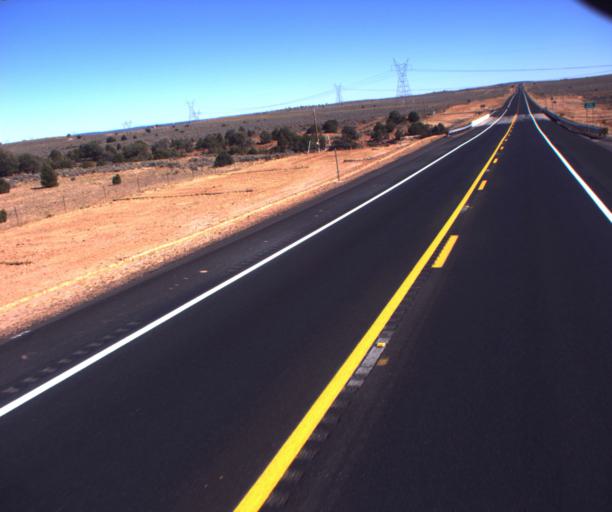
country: US
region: Arizona
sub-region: Apache County
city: Ganado
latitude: 35.7183
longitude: -109.4659
